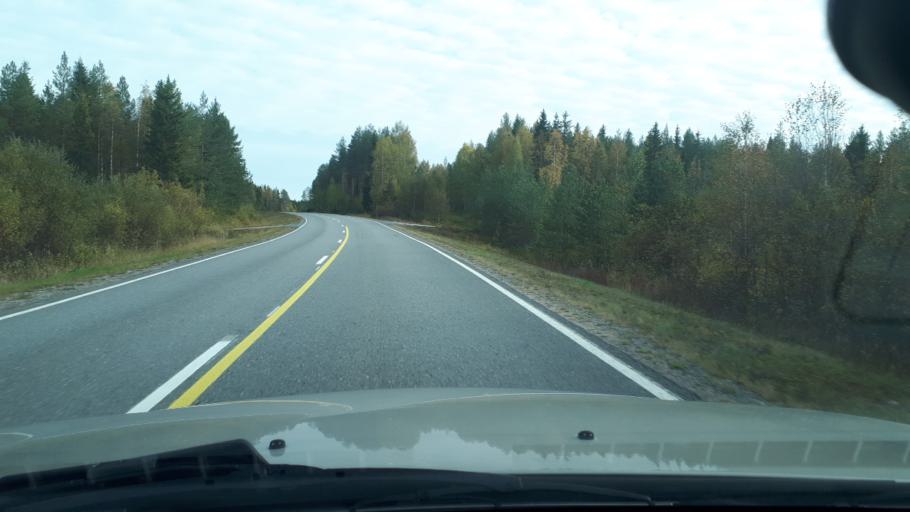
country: FI
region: Lapland
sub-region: Rovaniemi
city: Ranua
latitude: 65.9661
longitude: 25.9967
